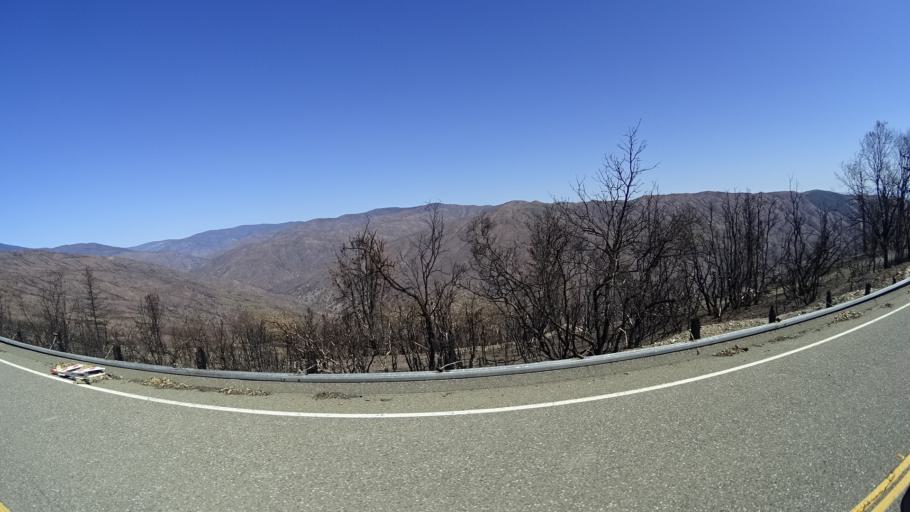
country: US
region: California
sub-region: Tehama County
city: Rancho Tehama Reserve
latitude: 39.6675
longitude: -122.6724
